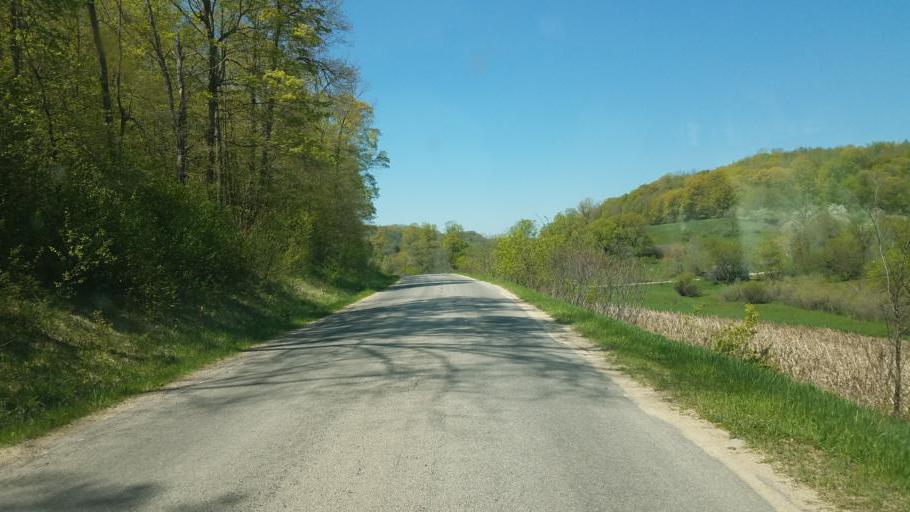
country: US
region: Wisconsin
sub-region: Vernon County
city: Hillsboro
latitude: 43.6245
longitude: -90.4790
